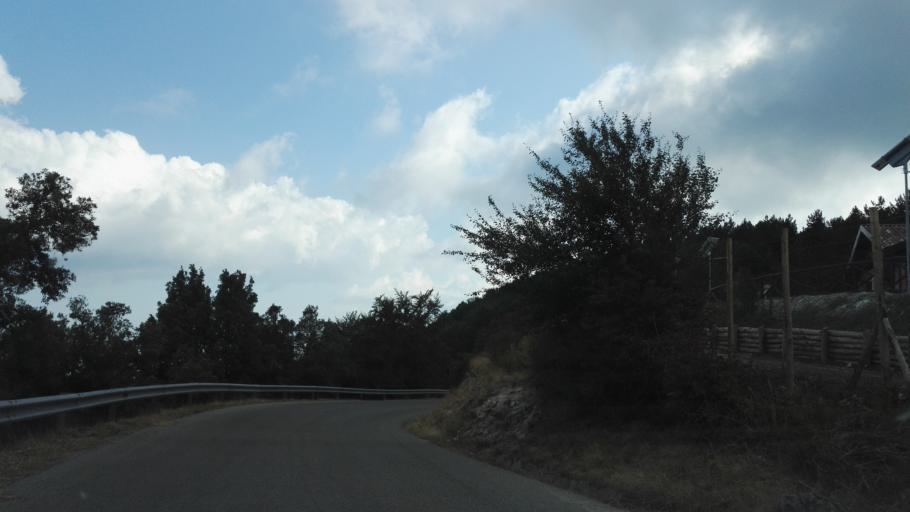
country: IT
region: Calabria
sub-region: Provincia di Vibo-Valentia
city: Nardodipace
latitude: 38.4895
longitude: 16.3440
